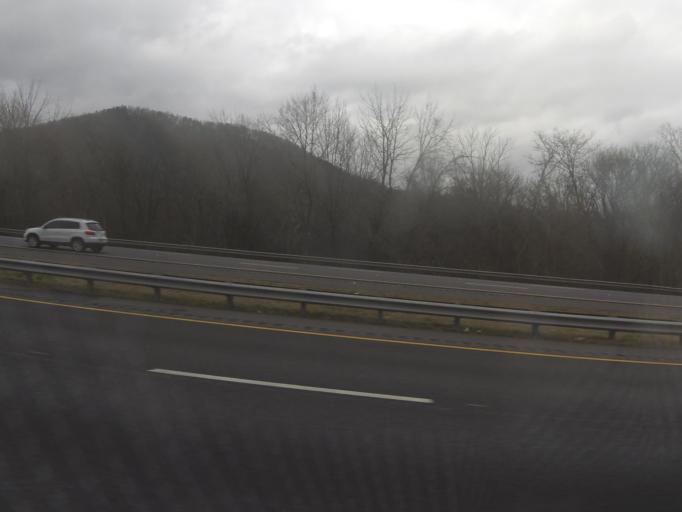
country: US
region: Georgia
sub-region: Whitfield County
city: Dalton
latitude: 34.8029
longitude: -85.0117
